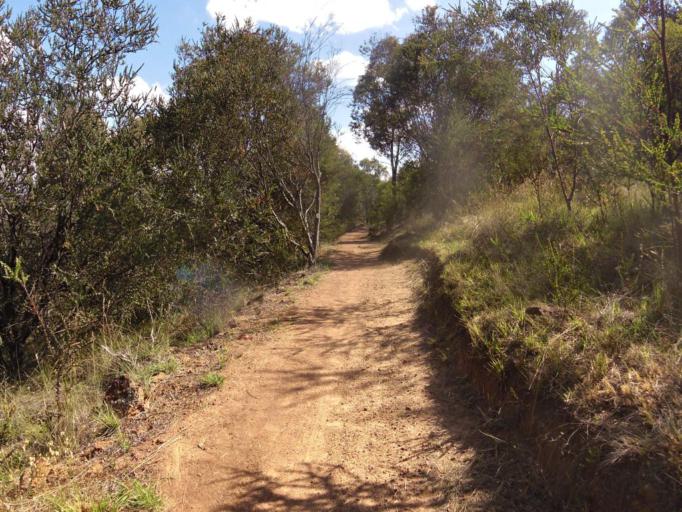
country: AU
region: Australian Capital Territory
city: Belconnen
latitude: -35.1612
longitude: 149.0755
